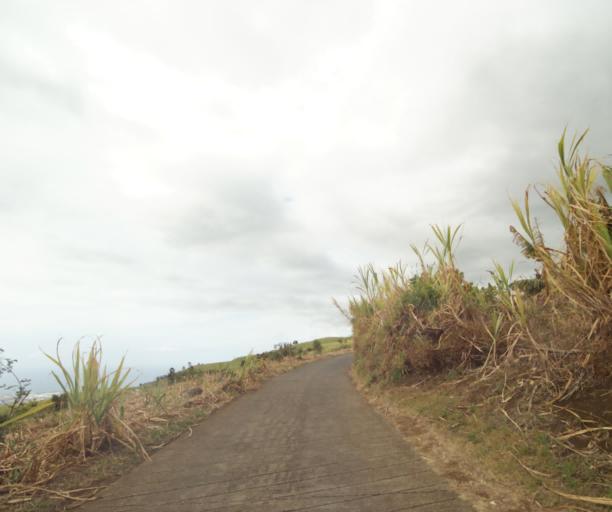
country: RE
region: Reunion
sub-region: Reunion
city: Saint-Paul
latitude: -21.0267
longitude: 55.3197
